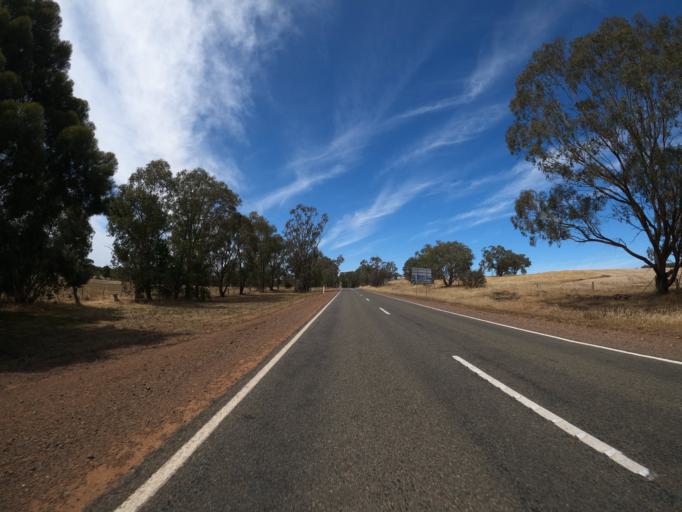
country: AU
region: Victoria
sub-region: Benalla
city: Benalla
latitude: -36.3206
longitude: 145.9585
